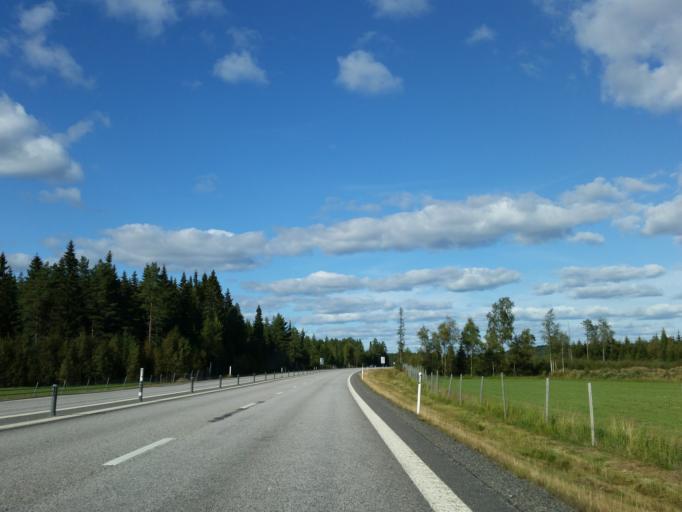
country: SE
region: Vaesterbotten
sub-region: Robertsfors Kommun
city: Robertsfors
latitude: 64.1210
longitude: 20.8825
